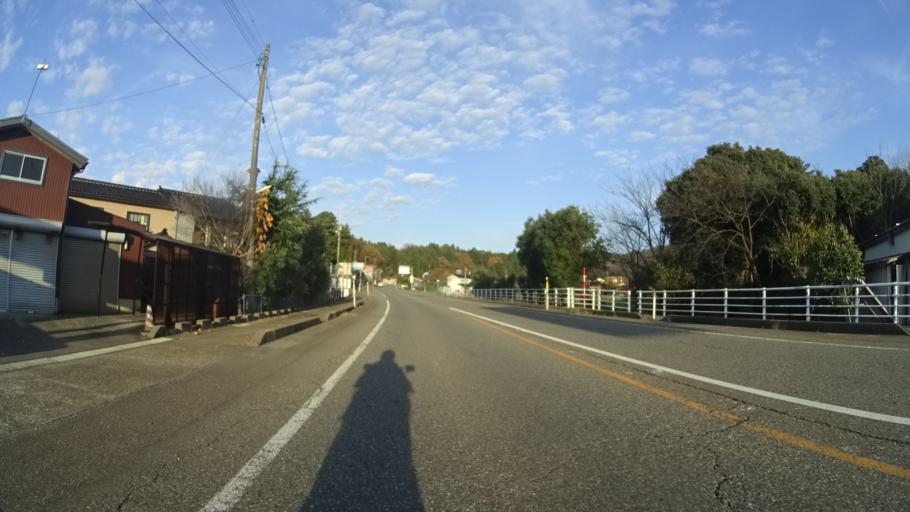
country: JP
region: Niigata
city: Kashiwazaki
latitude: 37.4050
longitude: 138.6385
